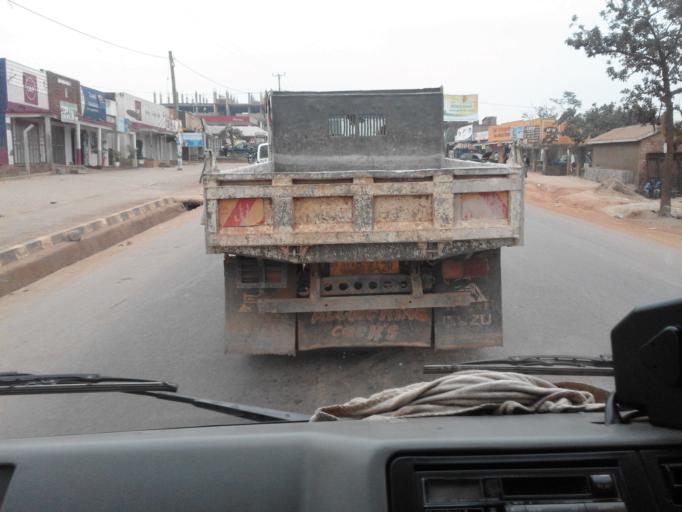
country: UG
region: Central Region
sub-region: Wakiso District
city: Bweyogerere
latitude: 0.3678
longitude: 32.7108
